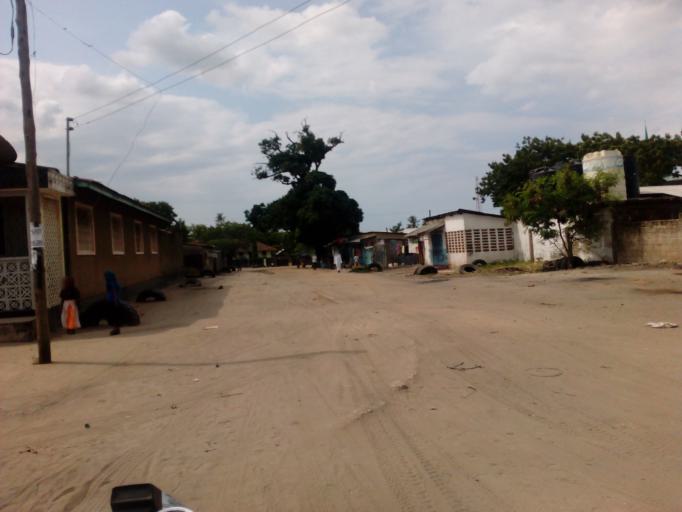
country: TZ
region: Dar es Salaam
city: Dar es Salaam
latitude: -6.8538
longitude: 39.2599
